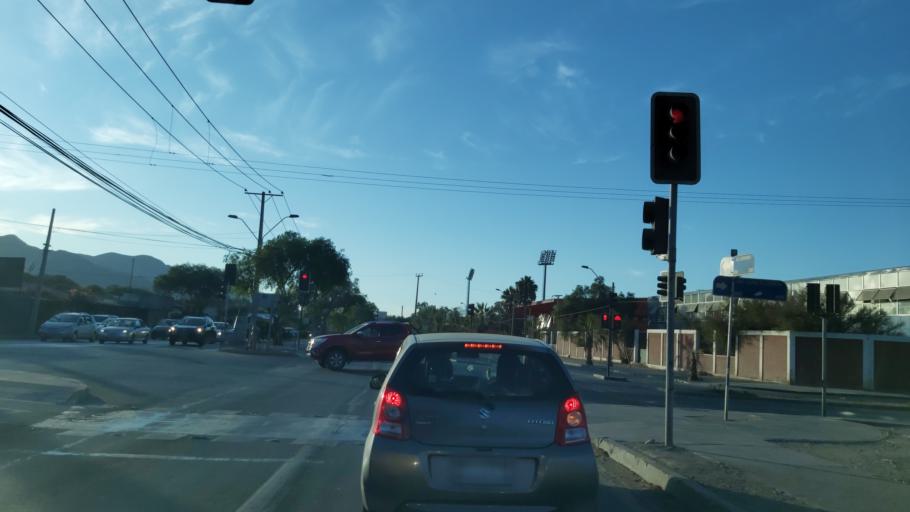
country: CL
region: Atacama
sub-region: Provincia de Copiapo
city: Copiapo
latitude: -27.3790
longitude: -70.3190
